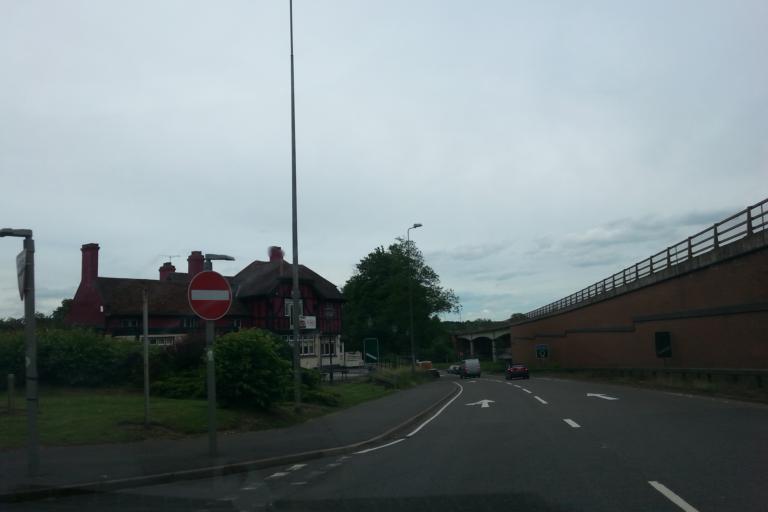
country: GB
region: England
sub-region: Solihull
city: Hampton in Arden
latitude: 52.4457
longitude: -1.6898
